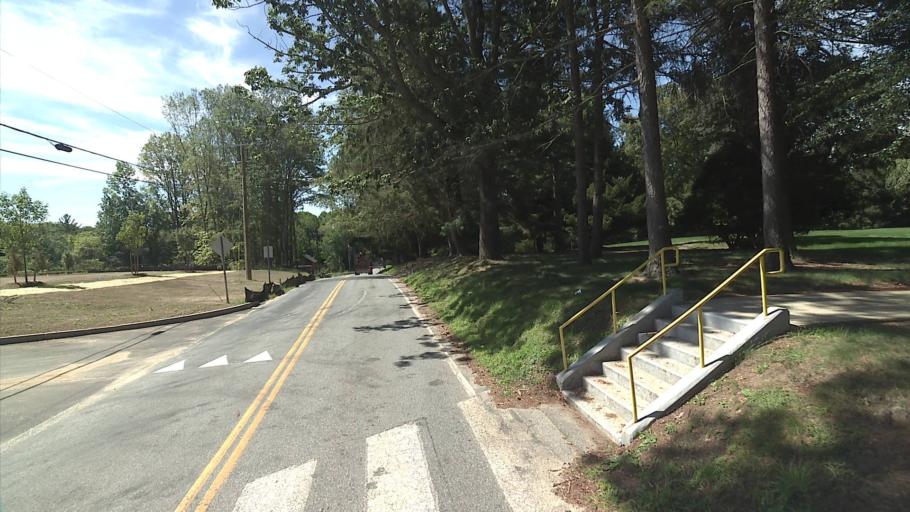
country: US
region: Connecticut
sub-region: Windham County
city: South Woodstock
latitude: 41.8750
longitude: -71.9738
